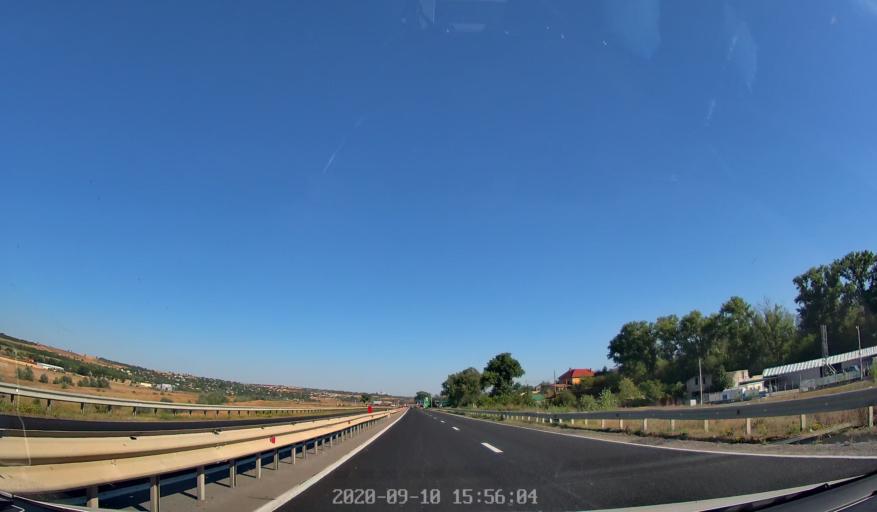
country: MD
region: Chisinau
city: Cricova
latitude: 47.1718
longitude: 28.8026
